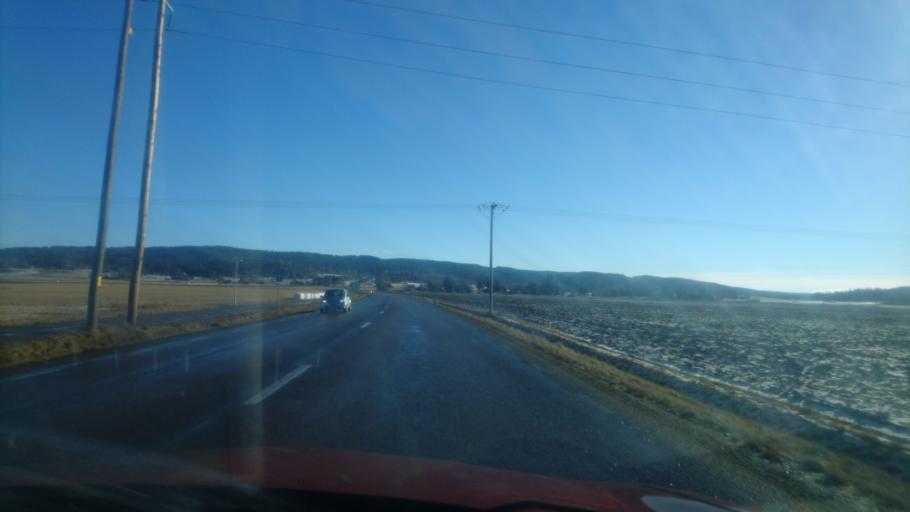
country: SE
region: Vaermland
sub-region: Sunne Kommun
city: Sunne
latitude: 59.8386
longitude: 13.1652
